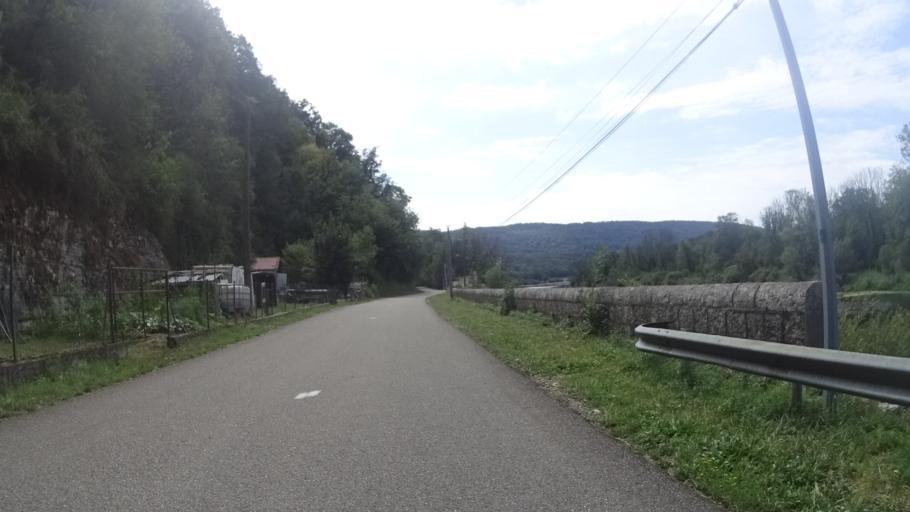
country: FR
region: Franche-Comte
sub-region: Departement du Doubs
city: Clerval
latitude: 47.3813
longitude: 6.5052
